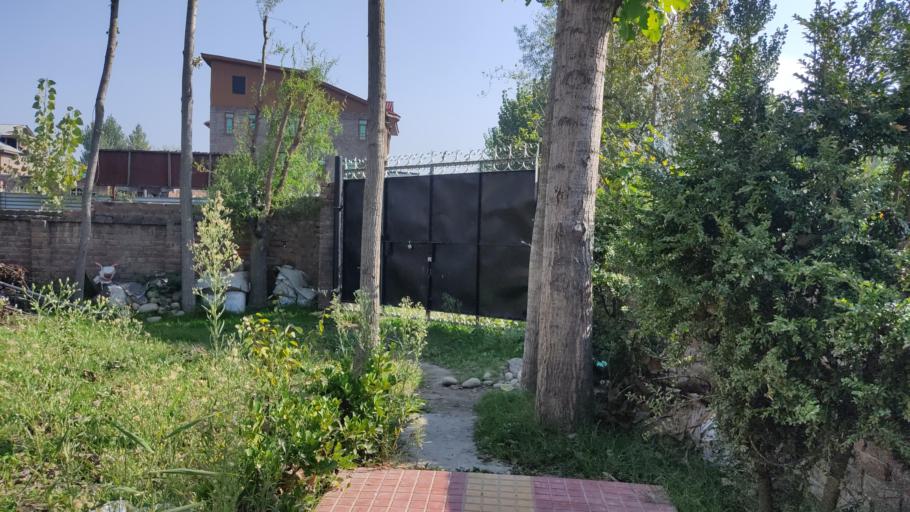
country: IN
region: Kashmir
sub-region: Baramula
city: Soyibug
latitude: 34.0536
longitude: 74.7428
